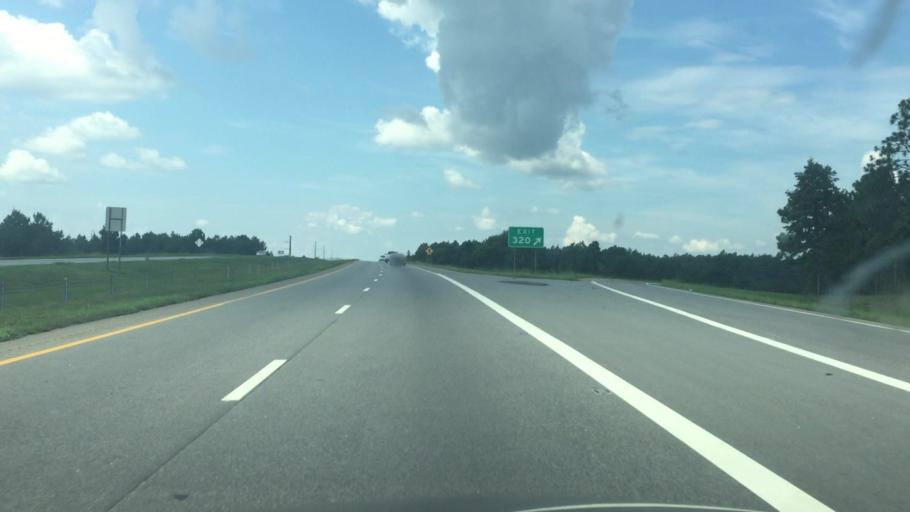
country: US
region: North Carolina
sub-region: Richmond County
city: Hamlet
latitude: 34.8658
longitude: -79.6673
